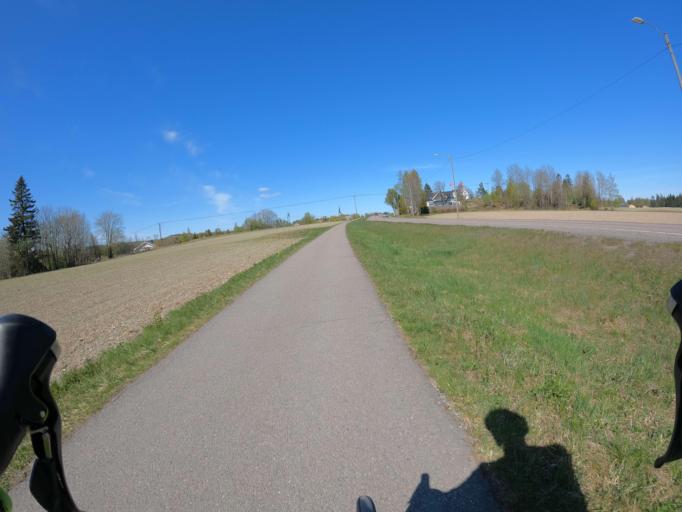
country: NO
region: Akershus
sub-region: Skedsmo
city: Lillestrom
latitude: 59.9868
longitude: 11.0476
